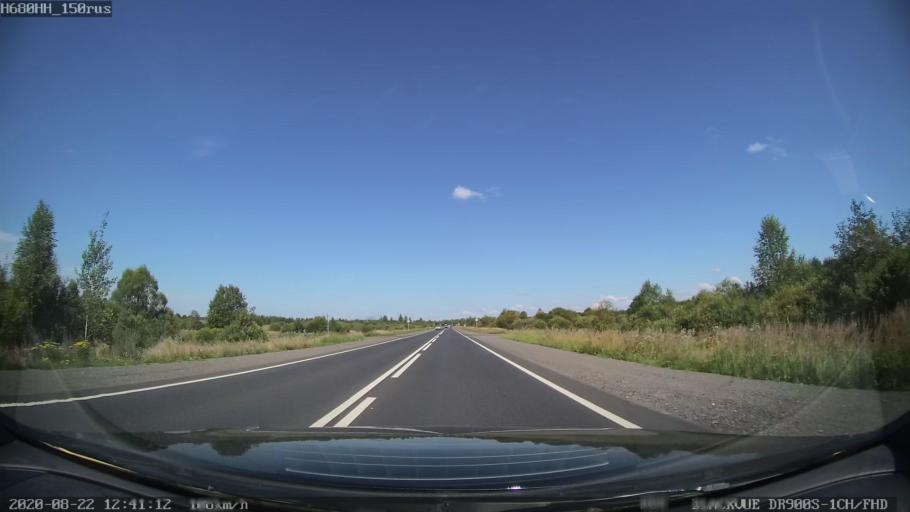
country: RU
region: Tverskaya
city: Rameshki
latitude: 57.3452
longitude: 36.0976
